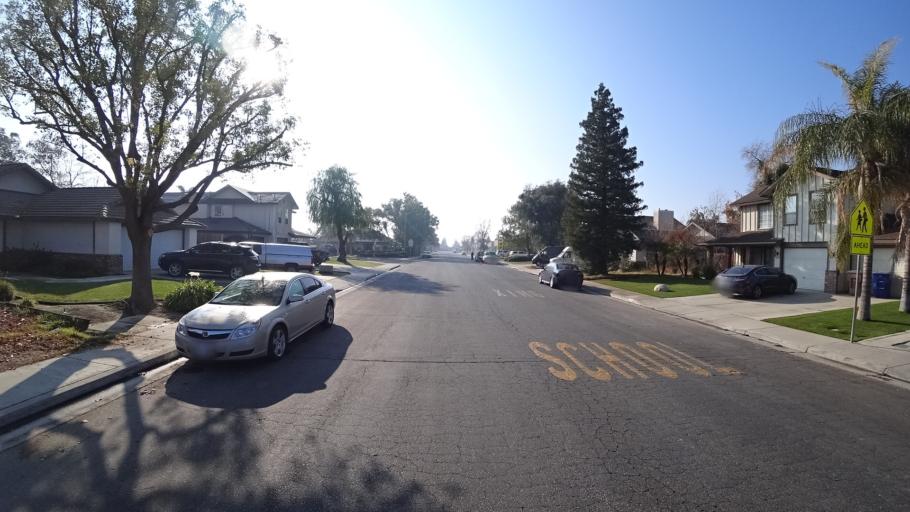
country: US
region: California
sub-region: Kern County
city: Greenacres
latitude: 35.3932
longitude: -119.1083
